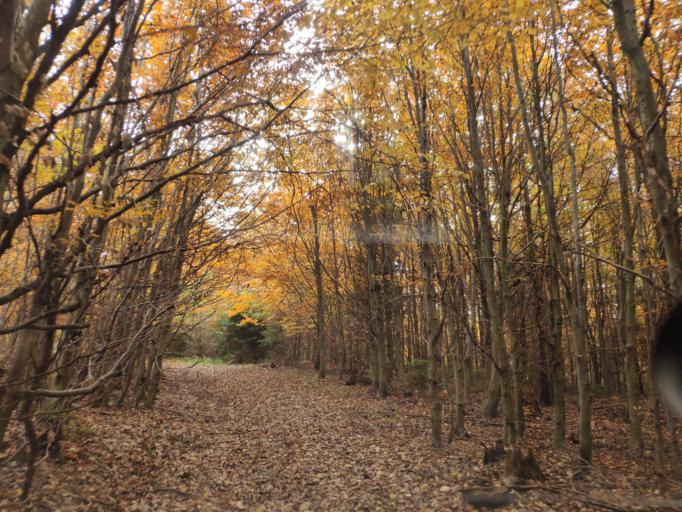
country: SK
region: Kosicky
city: Medzev
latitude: 48.7408
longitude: 20.9933
